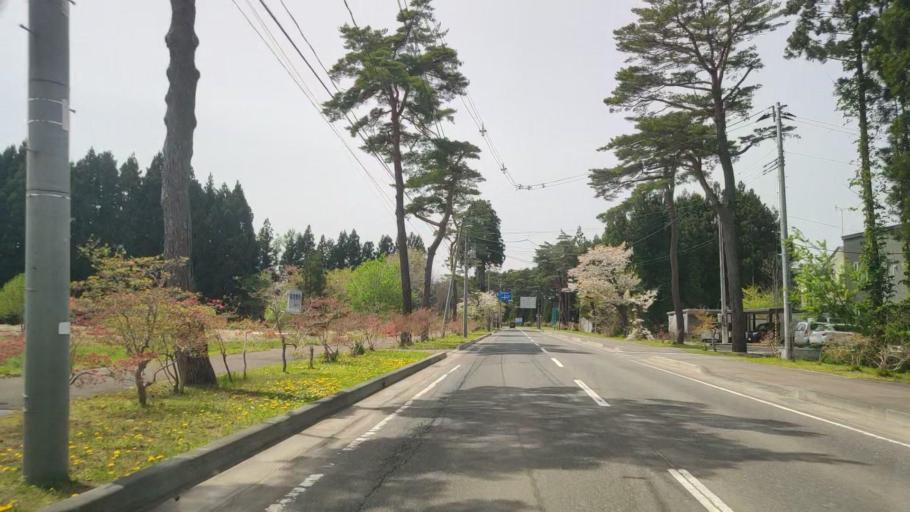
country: JP
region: Aomori
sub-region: Misawa Shi
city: Inuotose
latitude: 40.7155
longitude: 141.1460
